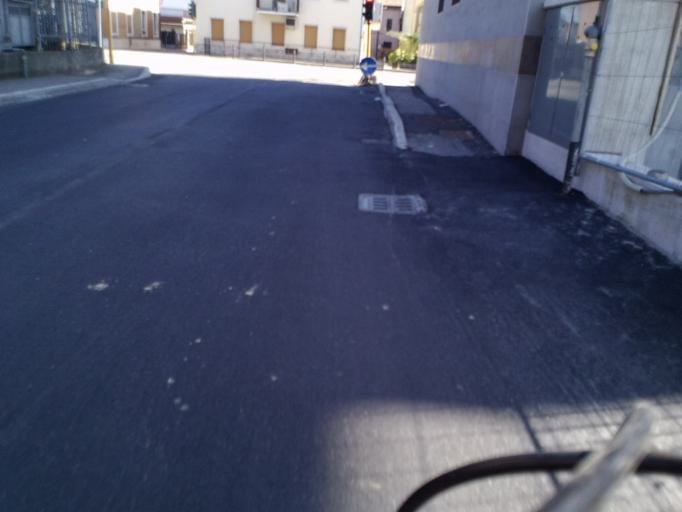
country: IT
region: Veneto
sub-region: Provincia di Verona
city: Dossobuono
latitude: 45.4062
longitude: 10.9290
